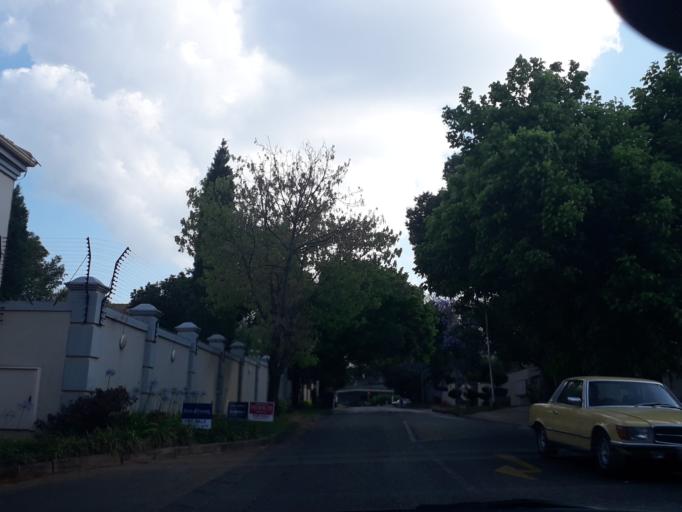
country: ZA
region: Gauteng
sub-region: City of Johannesburg Metropolitan Municipality
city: Johannesburg
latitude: -26.1452
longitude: 28.0556
